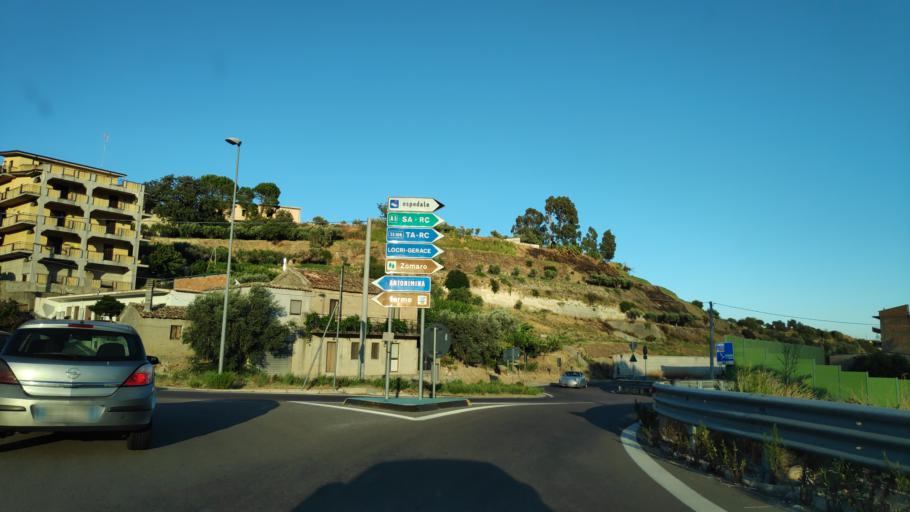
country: IT
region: Calabria
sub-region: Provincia di Reggio Calabria
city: Locri
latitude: 38.2384
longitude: 16.2357
